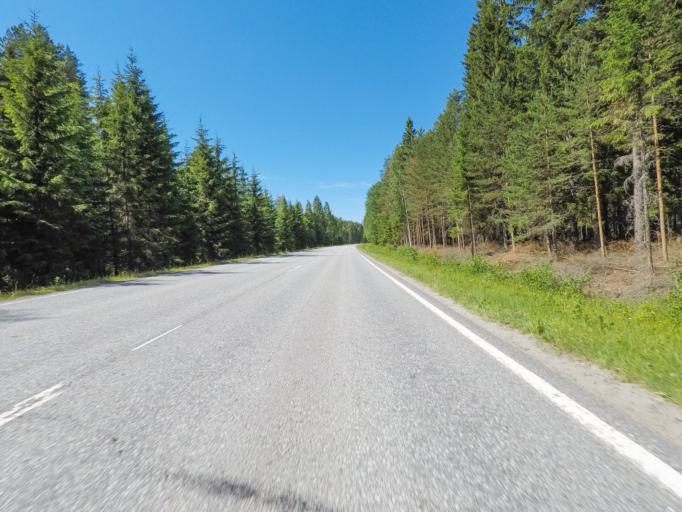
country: FI
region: Southern Savonia
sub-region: Savonlinna
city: Rantasalmi
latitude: 62.0148
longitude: 28.3839
